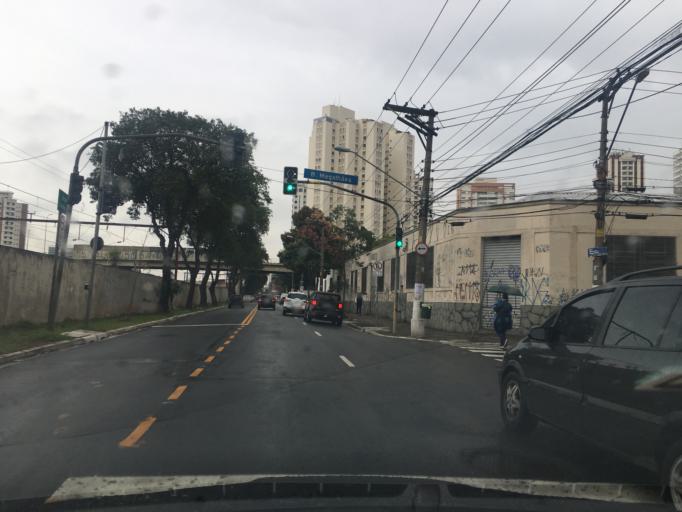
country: BR
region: Sao Paulo
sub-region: Sao Paulo
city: Sao Paulo
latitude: -23.5385
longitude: -46.5700
